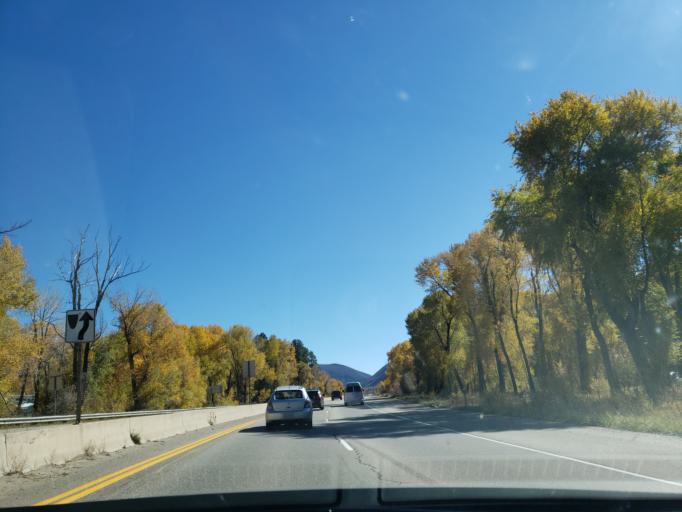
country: US
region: Colorado
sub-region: Eagle County
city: Basalt
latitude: 39.3630
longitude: -107.0322
